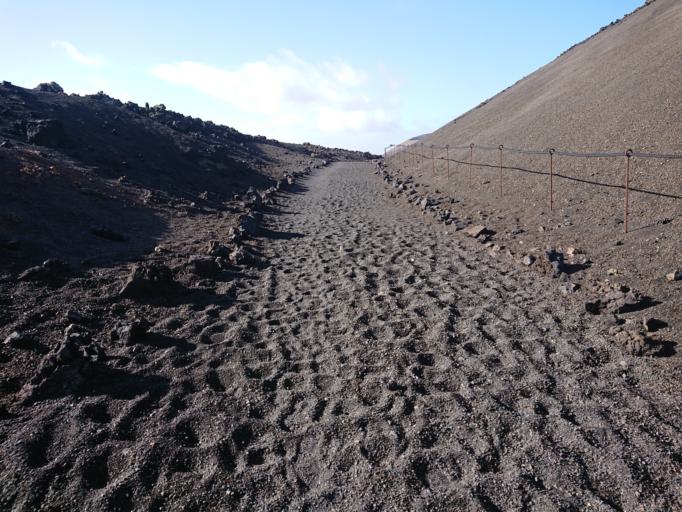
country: ES
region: Canary Islands
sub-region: Provincia de Las Palmas
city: Tias
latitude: 28.9911
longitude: -13.6903
